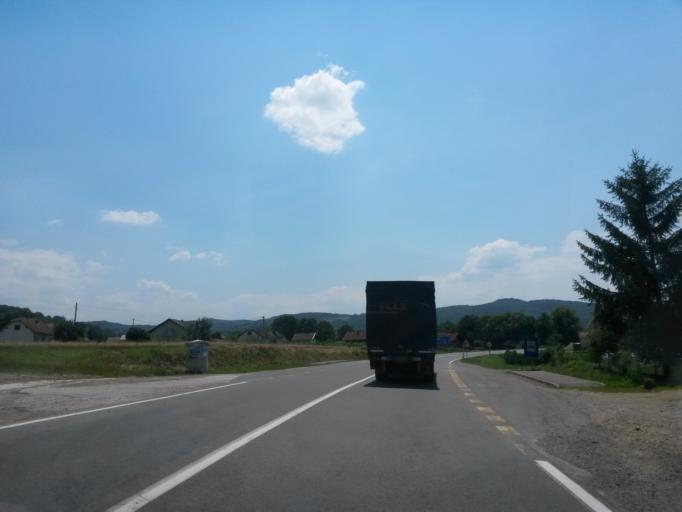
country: BA
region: Federation of Bosnia and Herzegovina
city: Lijesnica
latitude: 44.4913
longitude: 18.0848
